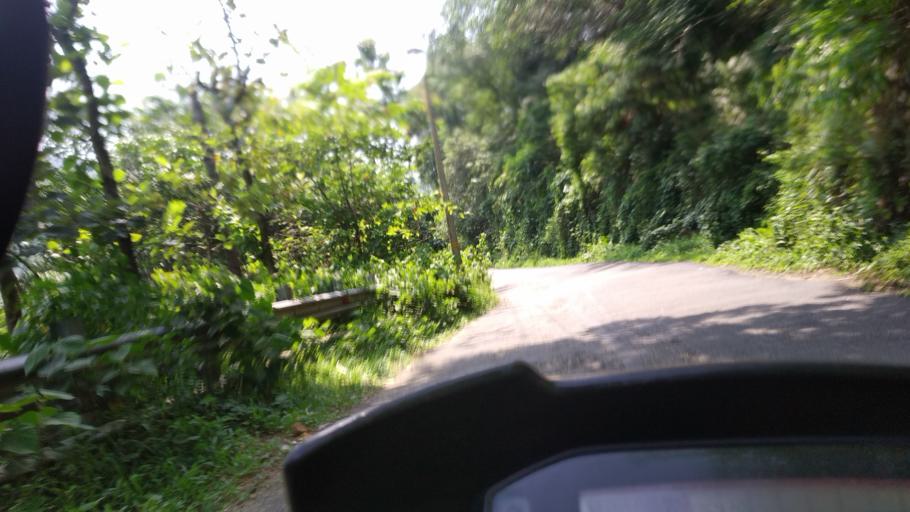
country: IN
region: Kerala
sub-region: Kottayam
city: Erattupetta
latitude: 9.6921
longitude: 76.8404
